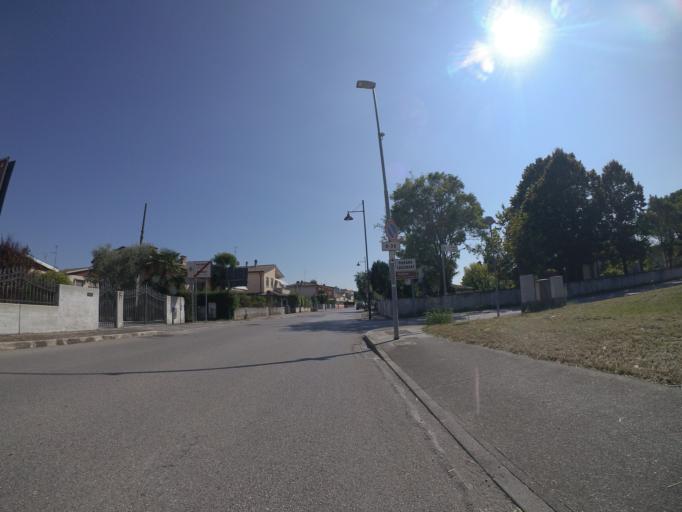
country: IT
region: Friuli Venezia Giulia
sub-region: Provincia di Udine
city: Marano Lagunare
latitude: 45.7692
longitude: 13.1682
